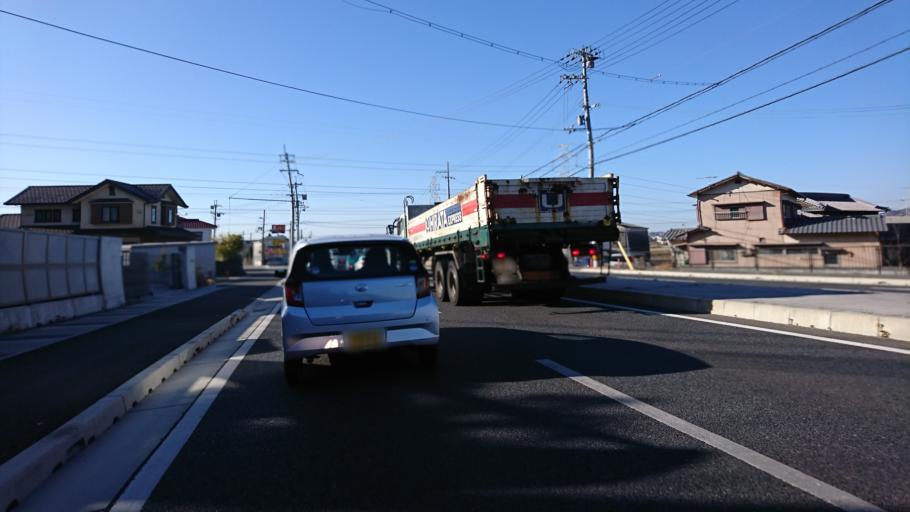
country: JP
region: Hyogo
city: Kakogawacho-honmachi
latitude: 34.8007
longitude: 134.8303
